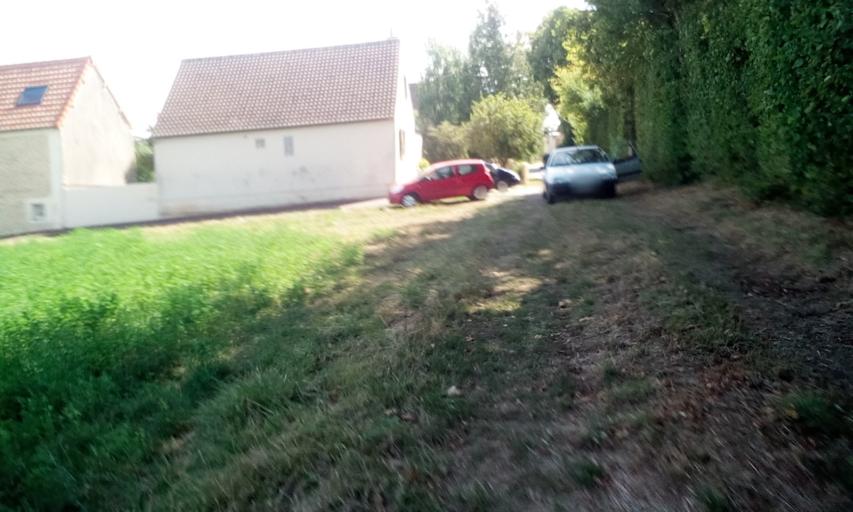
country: FR
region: Lower Normandy
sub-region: Departement du Calvados
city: Bully
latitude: 49.1123
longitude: -0.4327
